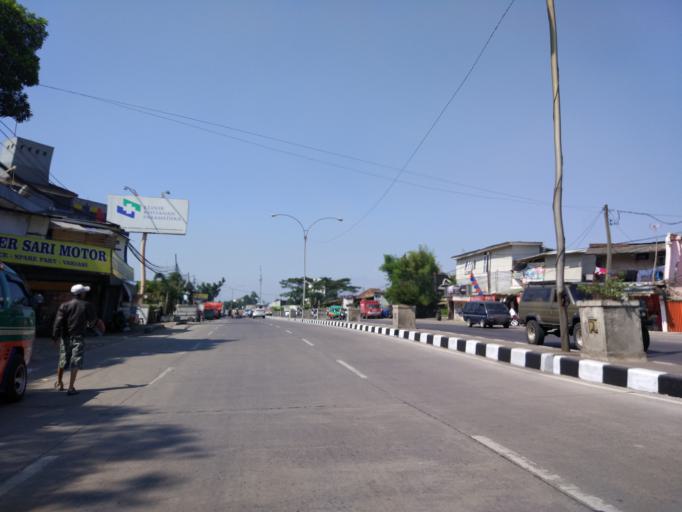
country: ID
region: West Java
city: Margahayukencana
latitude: -6.9330
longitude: 107.5769
